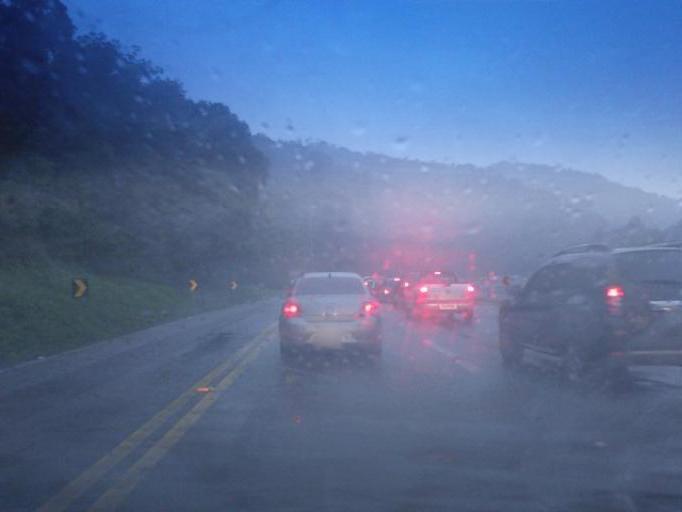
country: BR
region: Sao Paulo
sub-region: Juquitiba
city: Juquitiba
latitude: -24.0903
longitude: -47.2572
